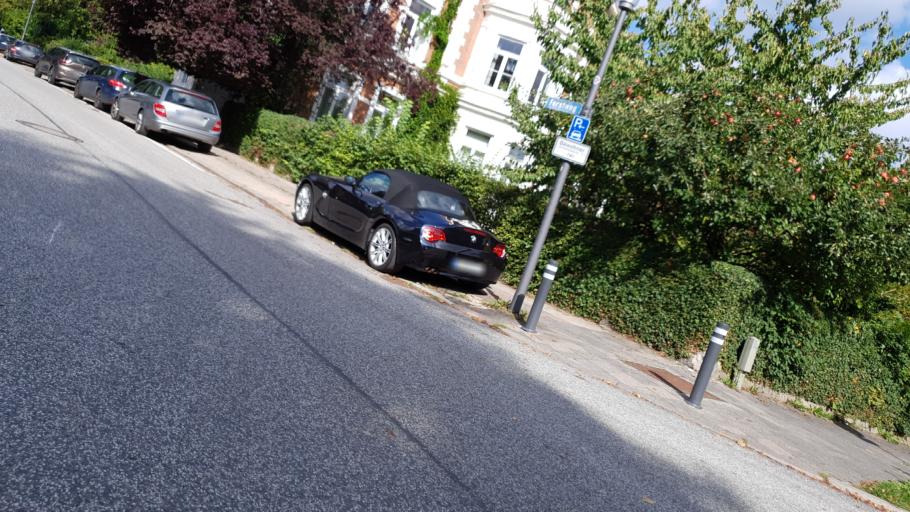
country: DE
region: Schleswig-Holstein
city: Kiel
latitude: 54.3346
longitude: 10.1442
